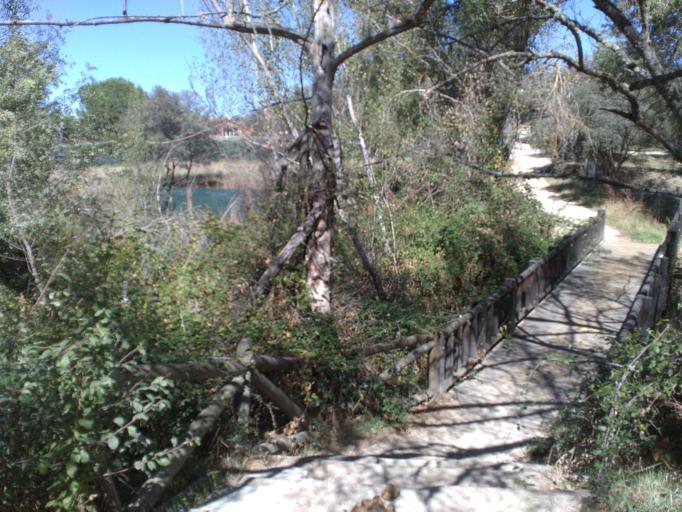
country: ES
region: Madrid
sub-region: Provincia de Madrid
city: Villanueva del Pardillo
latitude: 40.4473
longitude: -3.9665
